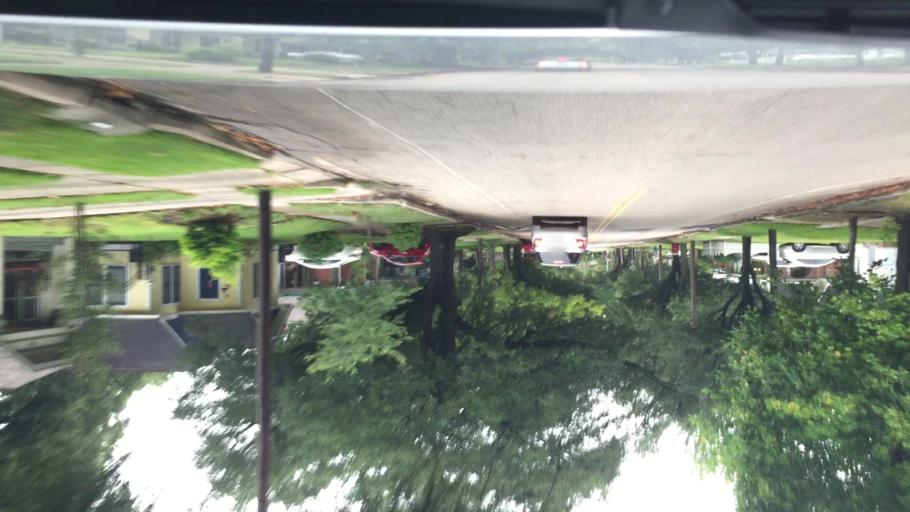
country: US
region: Texas
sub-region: Harris County
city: Houston
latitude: 29.7905
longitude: -95.3821
